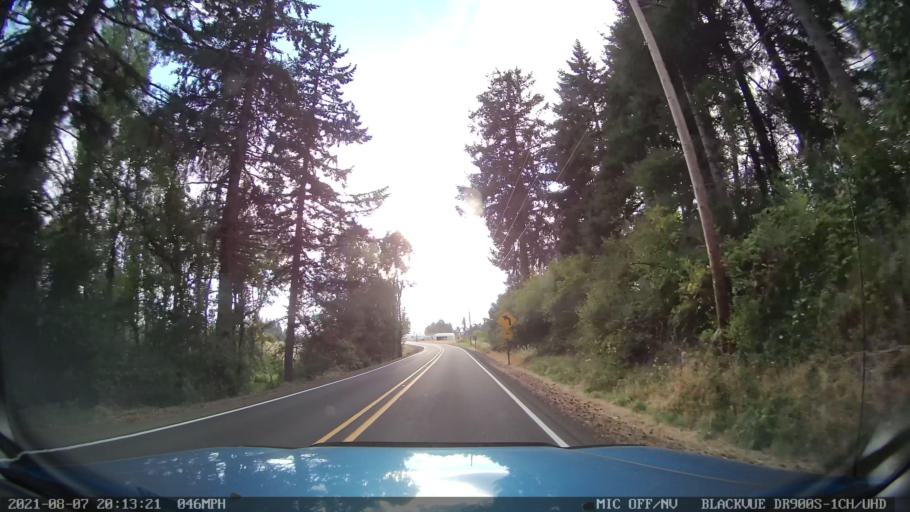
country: US
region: Oregon
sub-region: Marion County
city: Hayesville
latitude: 44.9568
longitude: -122.9224
